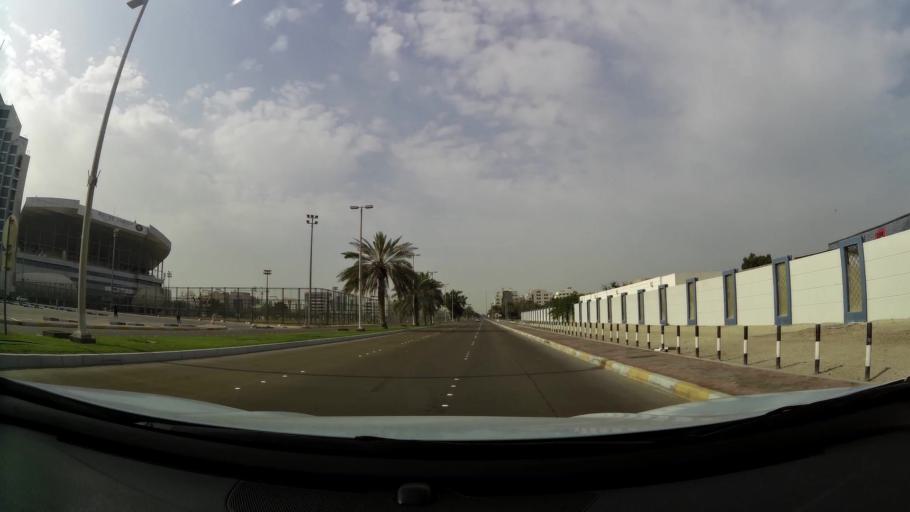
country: AE
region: Abu Dhabi
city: Abu Dhabi
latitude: 24.4553
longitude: 54.3914
